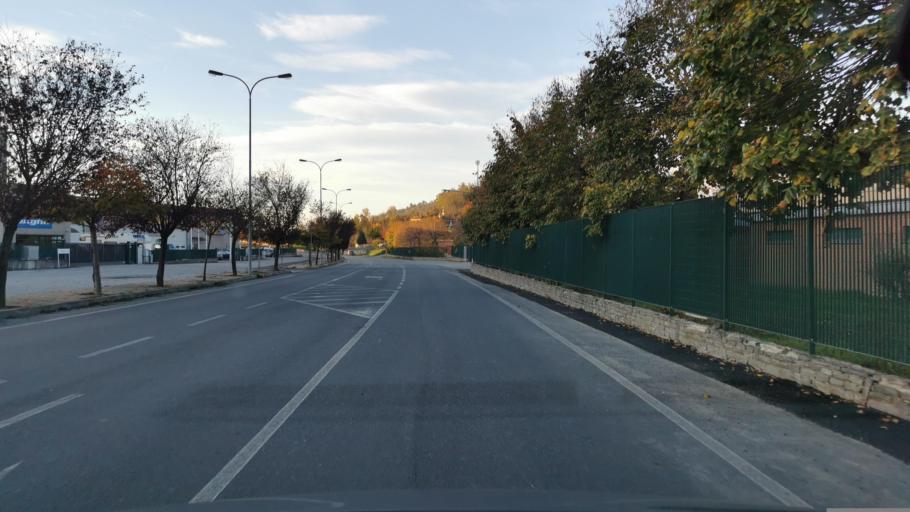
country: IT
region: Piedmont
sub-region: Provincia di Cuneo
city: Monchiero Borgonuovo
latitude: 44.5622
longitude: 7.9225
